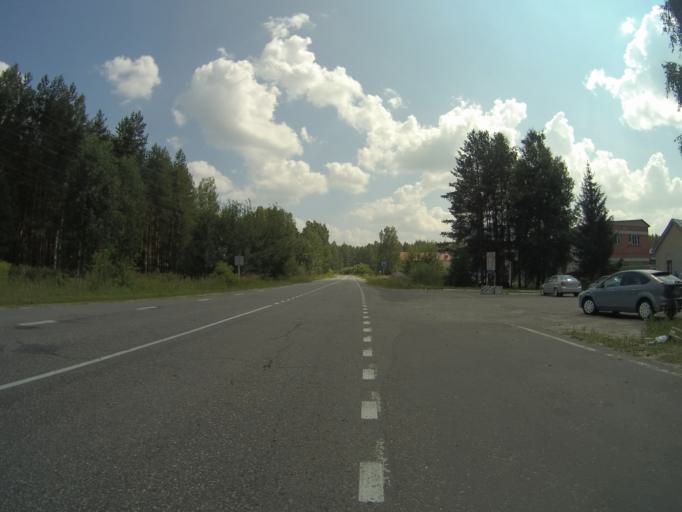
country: RU
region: Vladimir
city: Gus'-Khrustal'nyy
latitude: 55.6365
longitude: 40.7134
